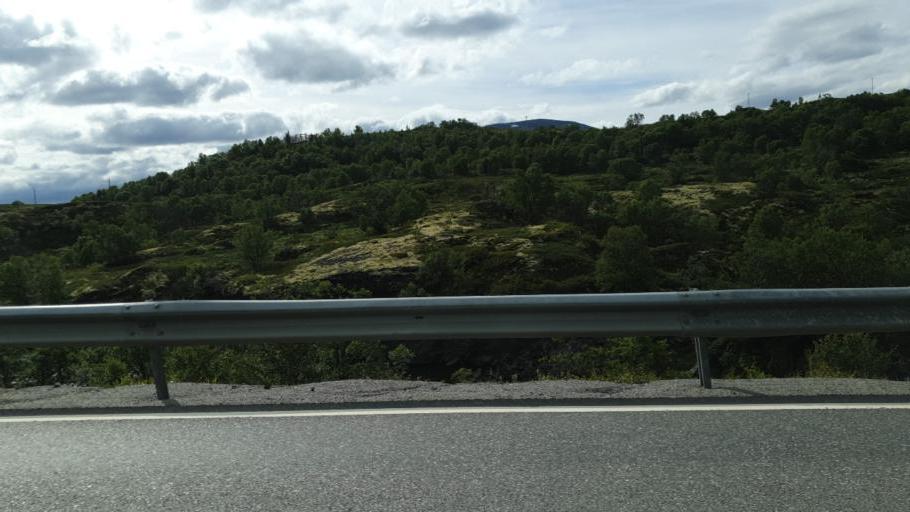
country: NO
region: Sor-Trondelag
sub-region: Oppdal
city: Oppdal
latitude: 62.2849
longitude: 9.6000
